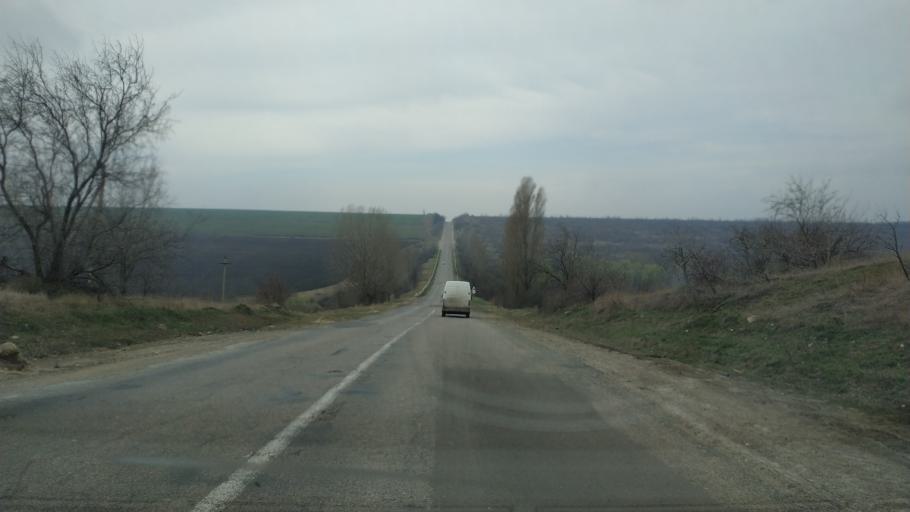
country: MD
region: Cahul
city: Cahul
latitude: 45.9595
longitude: 28.3833
